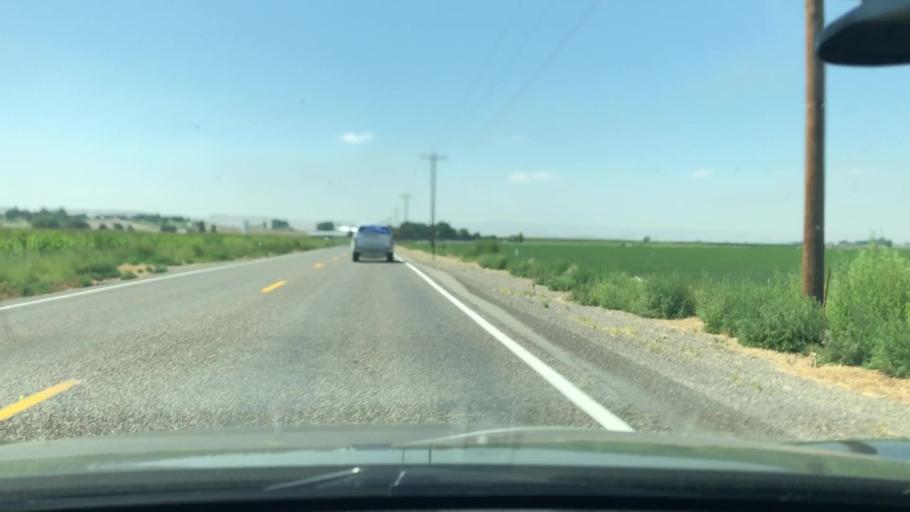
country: US
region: Idaho
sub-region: Owyhee County
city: Marsing
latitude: 43.5452
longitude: -116.8814
